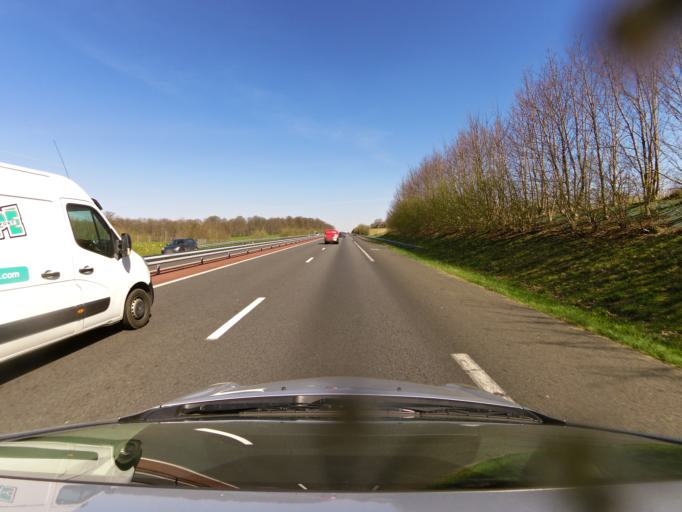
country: FR
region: Lower Normandy
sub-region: Departement de la Manche
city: Saint-Senier-sous-Avranches
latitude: 48.7611
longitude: -1.2782
